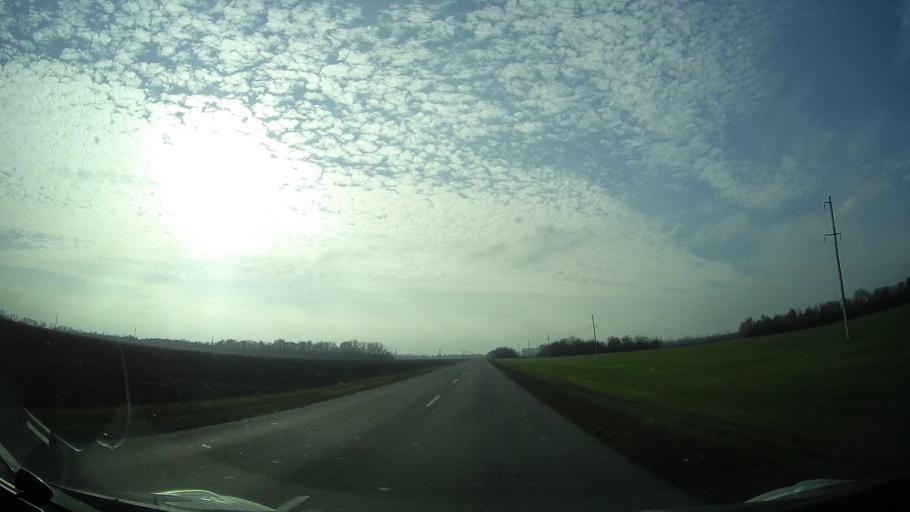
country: RU
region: Rostov
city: Mechetinskaya
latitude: 46.8002
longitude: 40.5137
